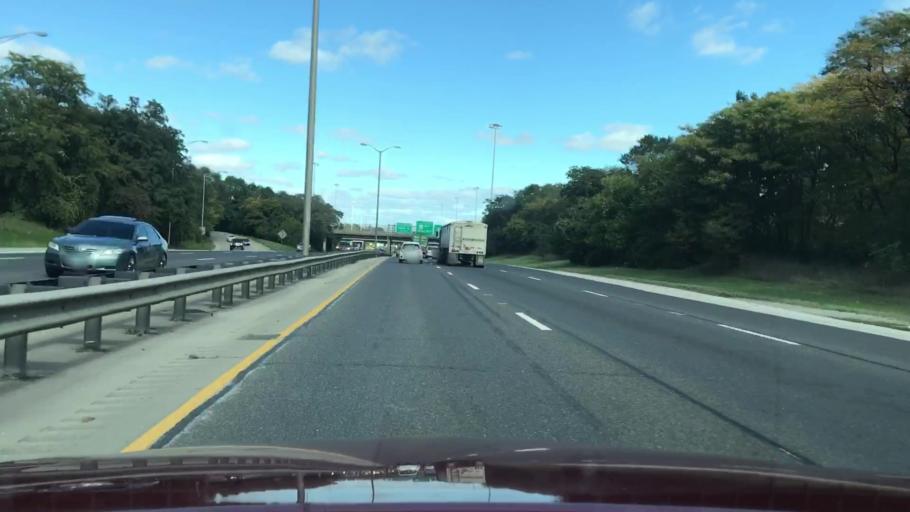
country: US
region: Illinois
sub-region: Cook County
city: Burnham
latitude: 41.6188
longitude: -87.5789
